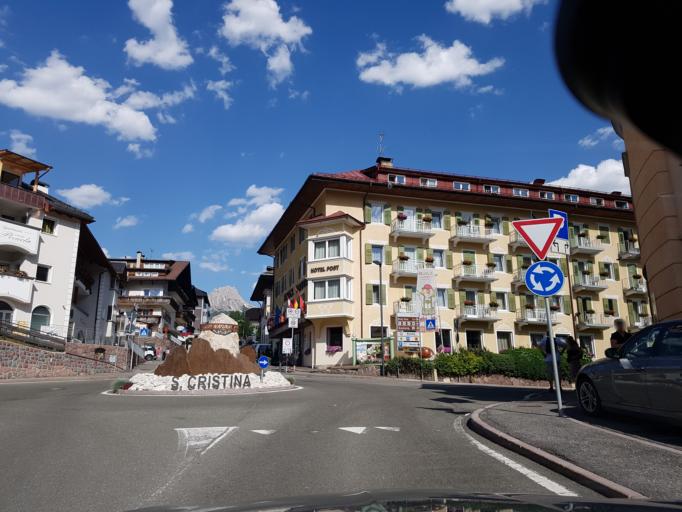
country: IT
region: Trentino-Alto Adige
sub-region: Bolzano
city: Santa Cristina Valgardena
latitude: 46.5580
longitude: 11.7221
